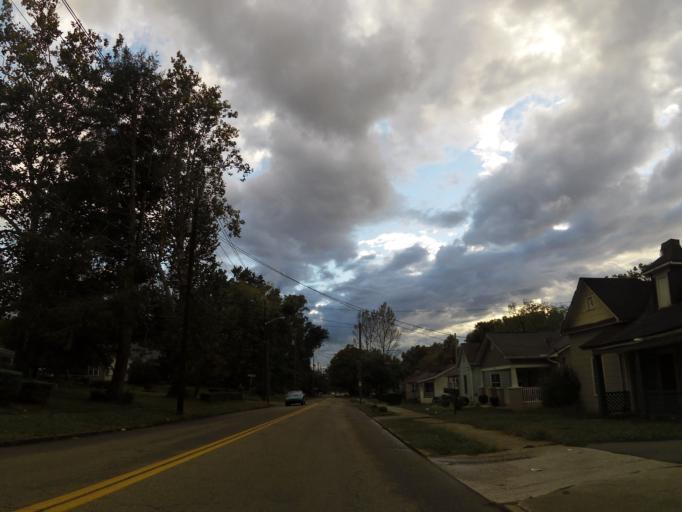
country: US
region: Tennessee
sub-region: Knox County
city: Knoxville
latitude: 35.9968
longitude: -83.8783
